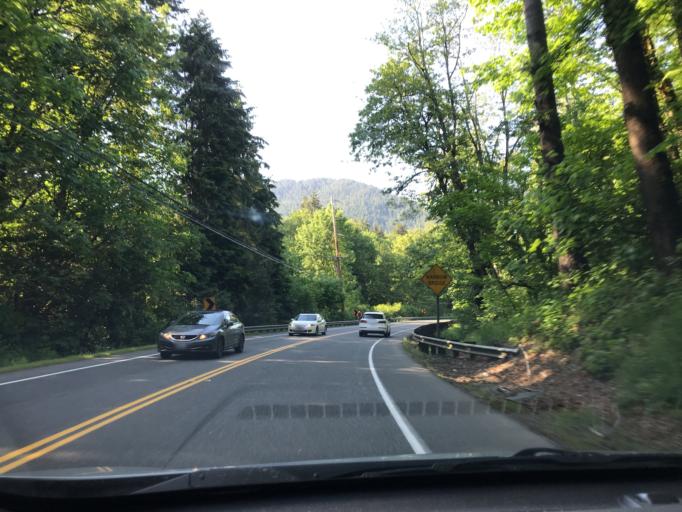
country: US
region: Washington
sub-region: King County
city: Mirrormont
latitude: 47.4785
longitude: -122.0291
